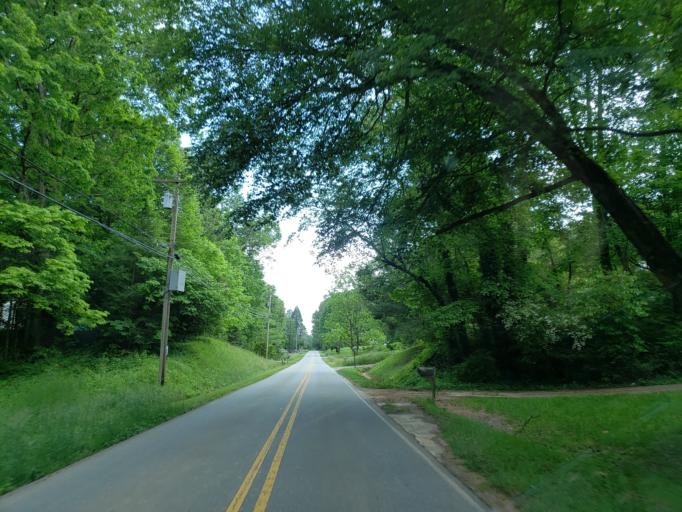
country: US
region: Georgia
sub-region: Fannin County
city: Blue Ridge
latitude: 34.8441
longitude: -84.3405
